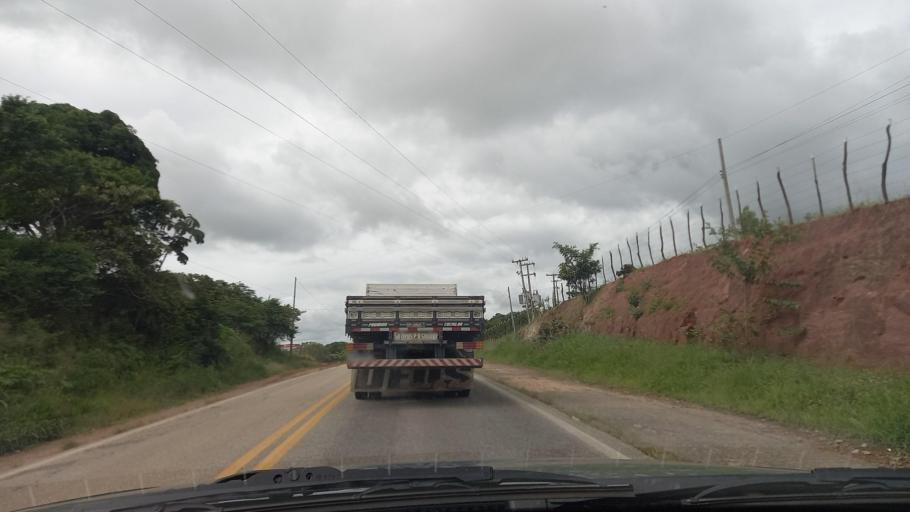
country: BR
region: Pernambuco
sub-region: Canhotinho
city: Canhotinho
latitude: -8.8582
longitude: -36.1760
